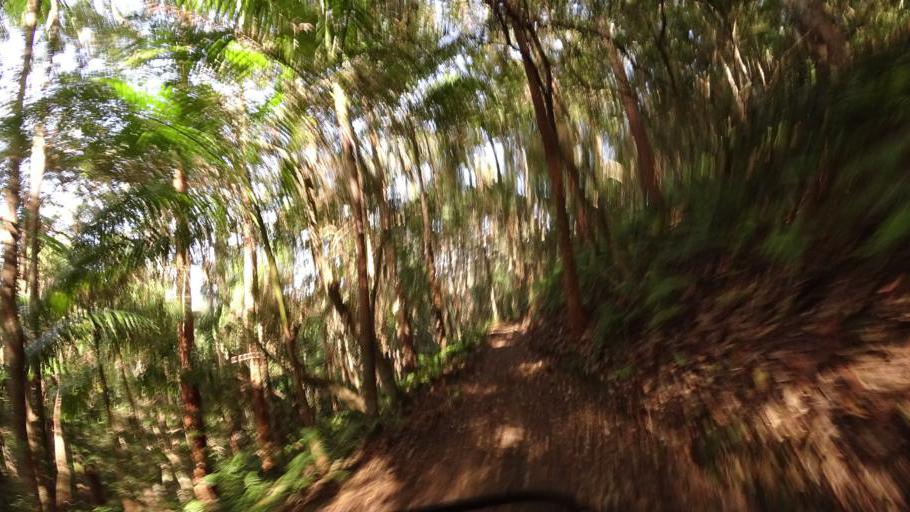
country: AU
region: Queensland
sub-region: Moreton Bay
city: Highvale
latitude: -27.4050
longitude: 152.8035
